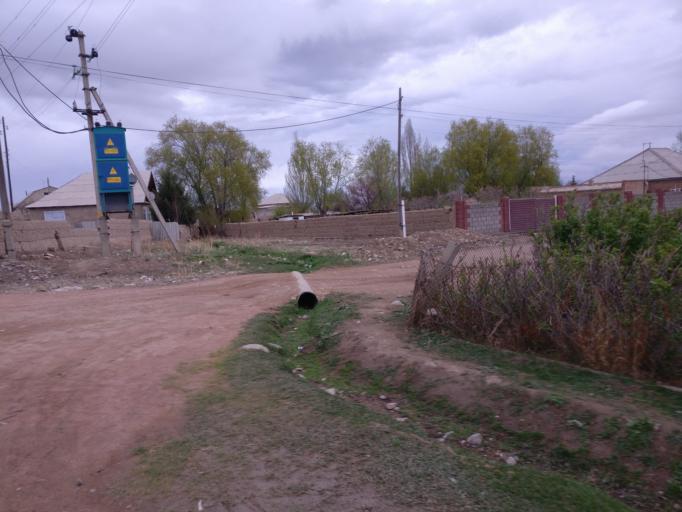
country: KG
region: Ysyk-Koel
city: Bokombayevskoye
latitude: 42.1110
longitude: 76.9812
